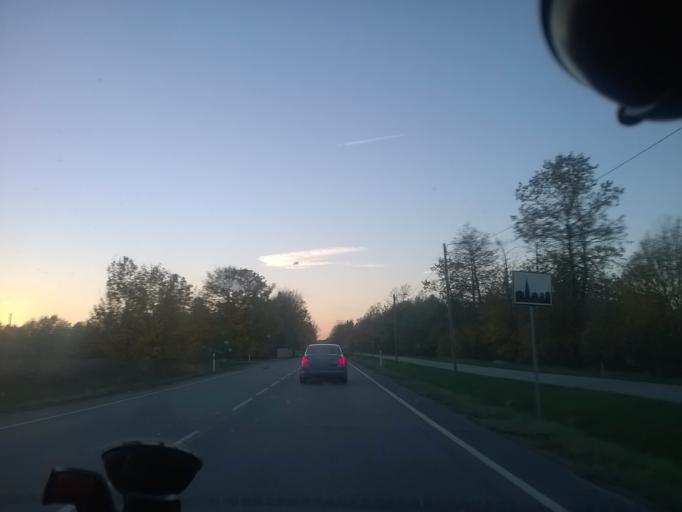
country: EE
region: Laeaene
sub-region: Ridala Parish
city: Uuemoisa
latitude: 58.9558
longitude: 23.7532
